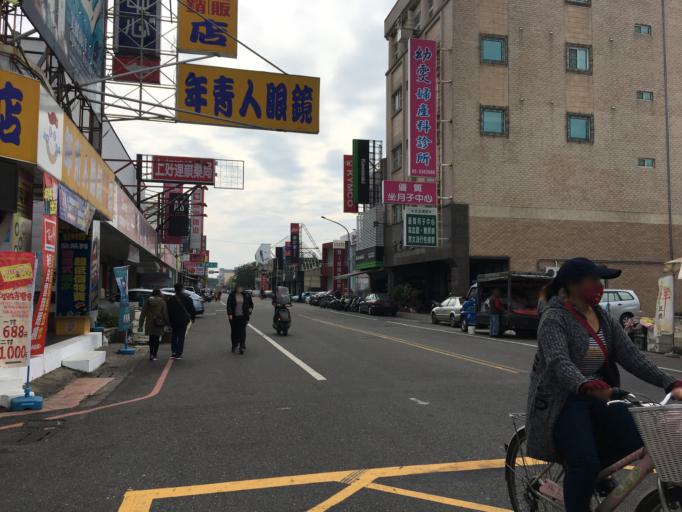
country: TW
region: Taiwan
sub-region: Yunlin
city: Douliu
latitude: 23.7042
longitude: 120.5371
